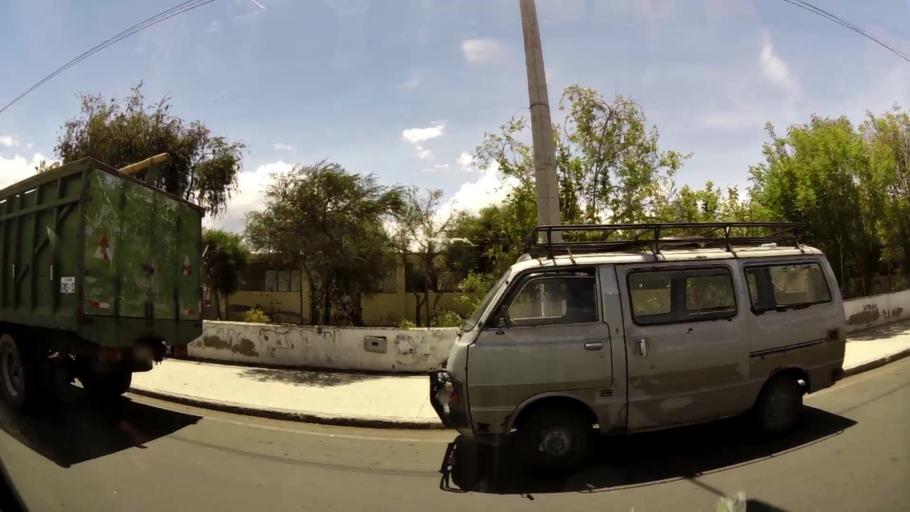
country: EC
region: Chimborazo
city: Riobamba
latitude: -1.6876
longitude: -78.6333
